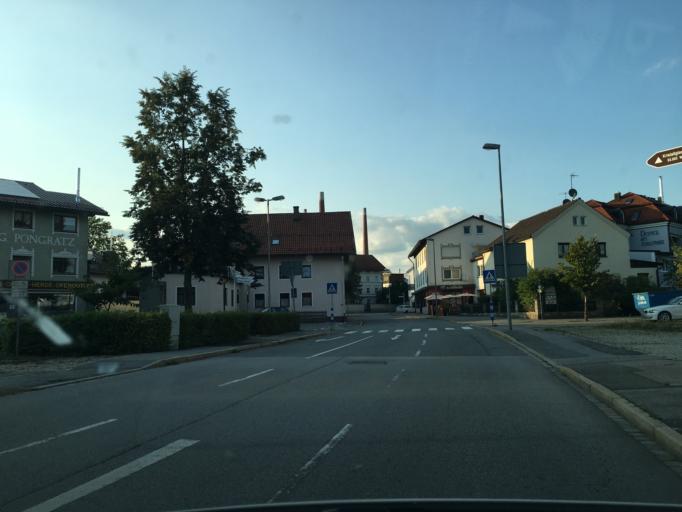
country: DE
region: Bavaria
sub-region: Lower Bavaria
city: Zwiesel
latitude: 49.0141
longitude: 13.2277
